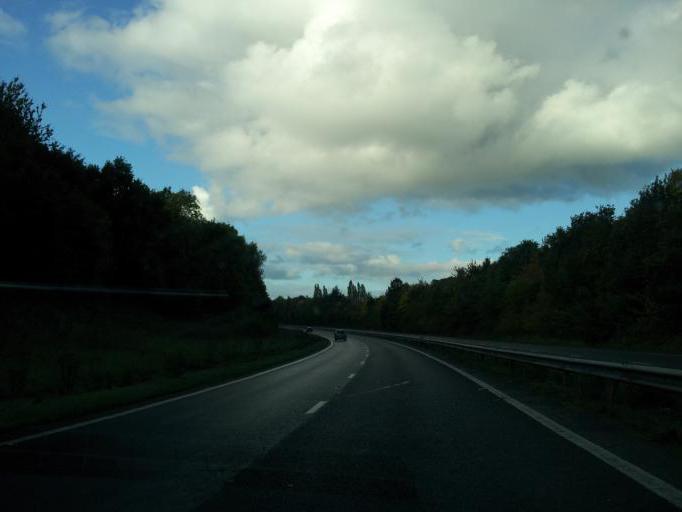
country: GB
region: England
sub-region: Norfolk
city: Brundall
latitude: 52.6386
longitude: 1.4474
